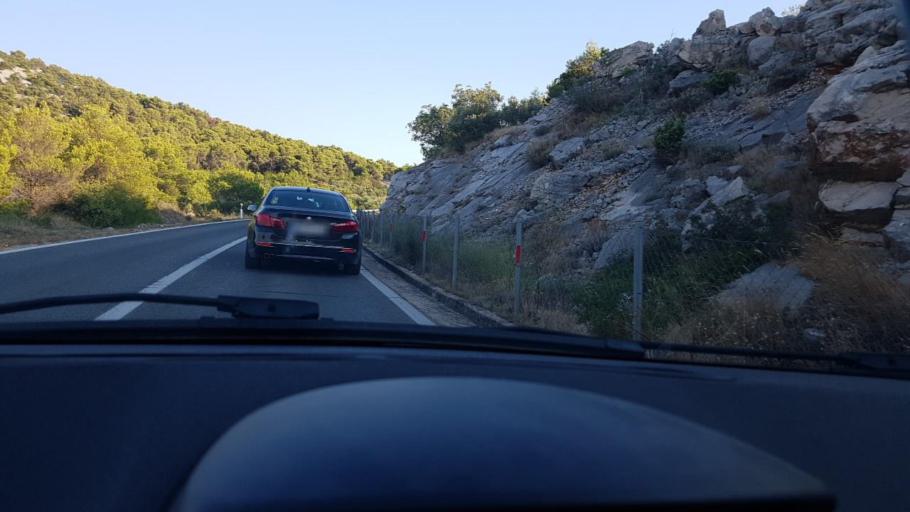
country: HR
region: Sibensko-Kniniska
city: Murter
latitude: 43.8029
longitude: 15.6109
